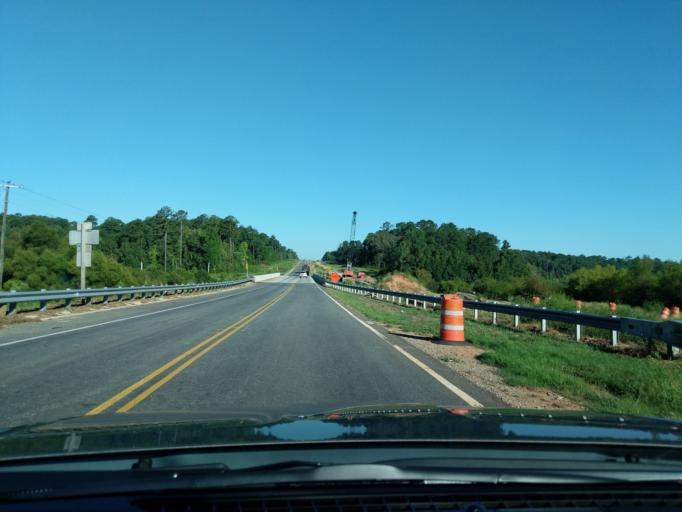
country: US
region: Georgia
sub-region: McDuffie County
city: Thomson
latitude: 33.5809
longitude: -82.5295
